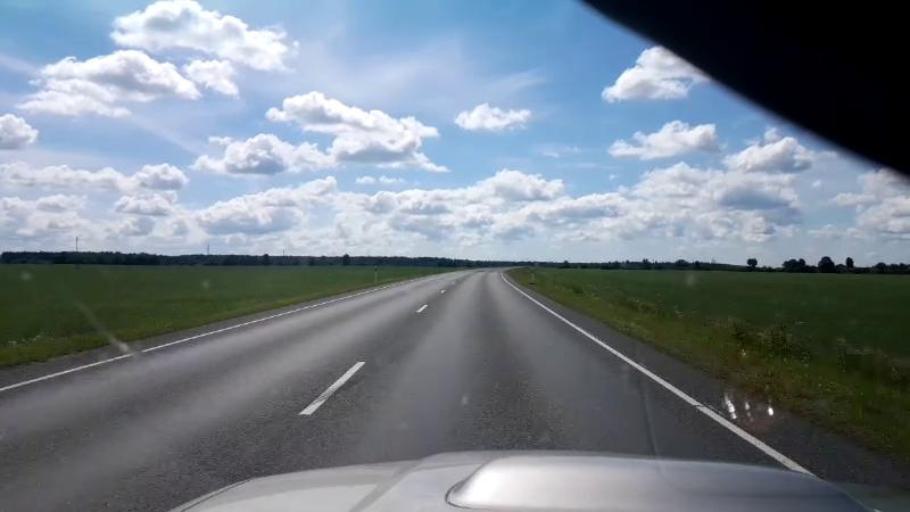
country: EE
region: Jaervamaa
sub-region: Jaerva-Jaani vald
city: Jarva-Jaani
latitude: 59.1493
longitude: 25.7701
